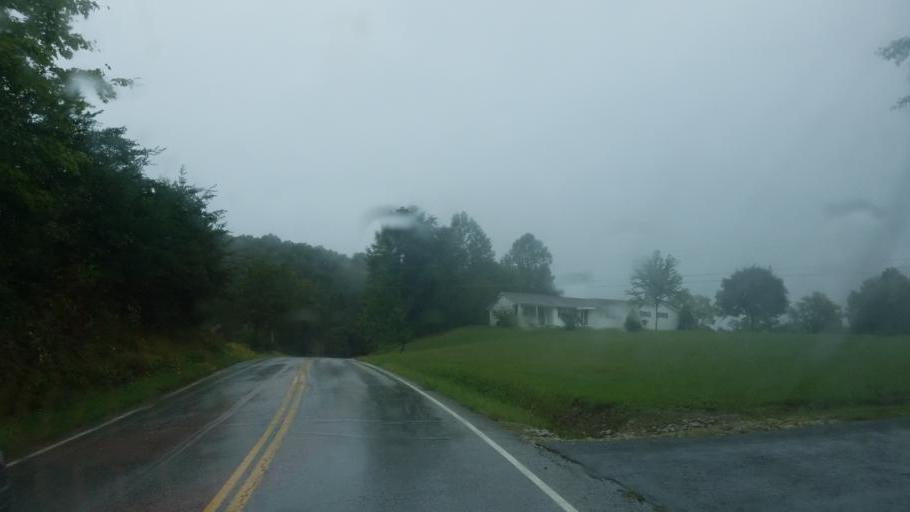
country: US
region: Kentucky
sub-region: Greenup County
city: South Shore
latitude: 38.6426
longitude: -82.9324
